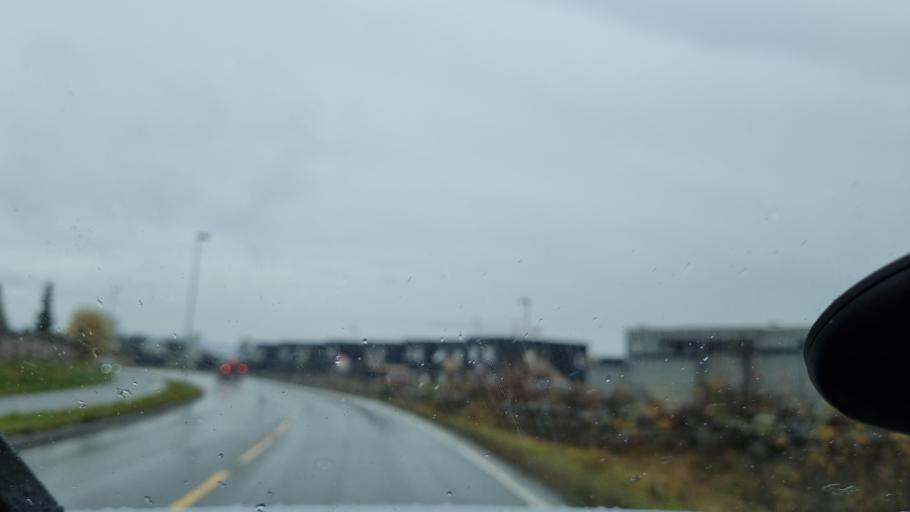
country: NO
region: Hedmark
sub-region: Hamar
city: Hamar
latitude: 60.8145
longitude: 11.0618
